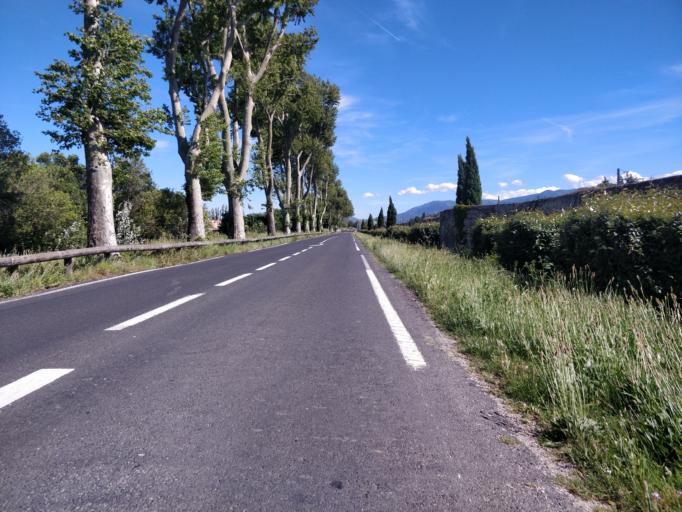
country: FR
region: Languedoc-Roussillon
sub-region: Departement des Pyrenees-Orientales
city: Corneilla-del-Vercol
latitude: 42.6215
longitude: 2.9518
